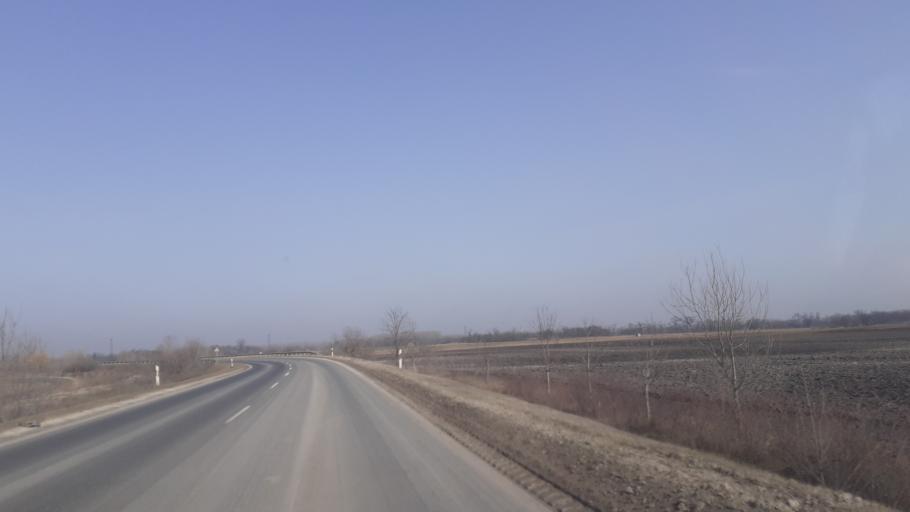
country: HU
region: Pest
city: Bugyi
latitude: 47.2355
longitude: 19.1193
